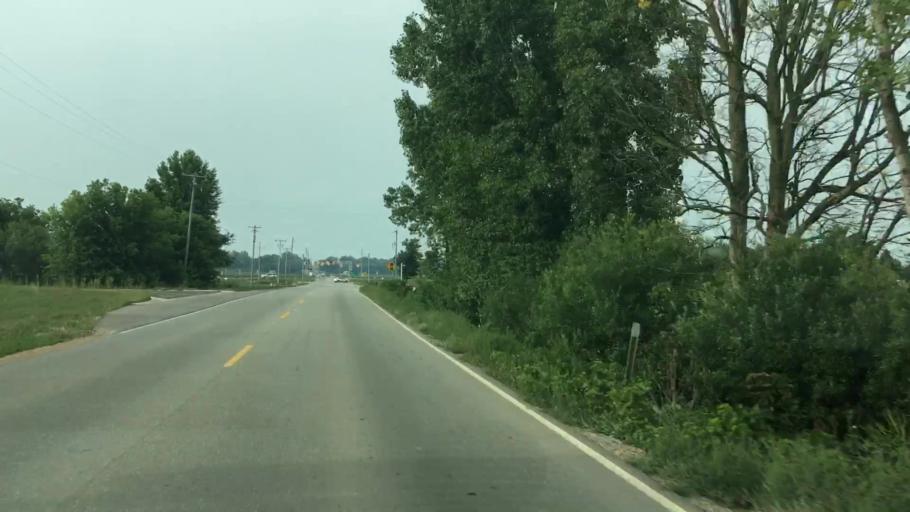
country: US
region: Michigan
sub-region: Ottawa County
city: Hudsonville
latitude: 42.8498
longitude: -85.9006
